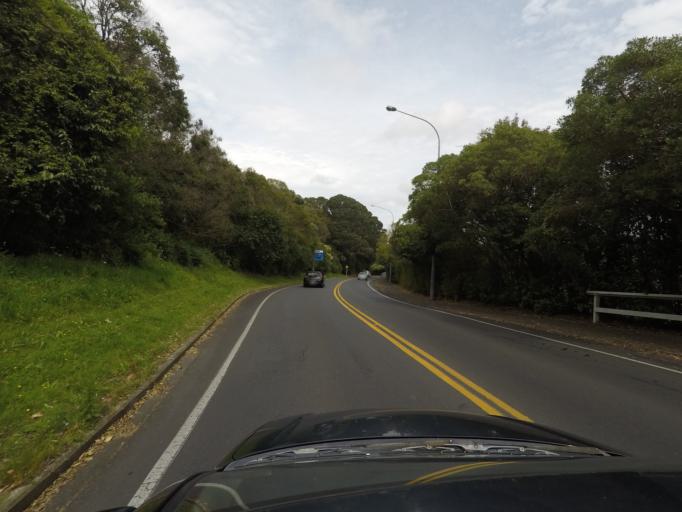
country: NZ
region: Auckland
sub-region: Auckland
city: Auckland
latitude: -36.8590
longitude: 174.8103
